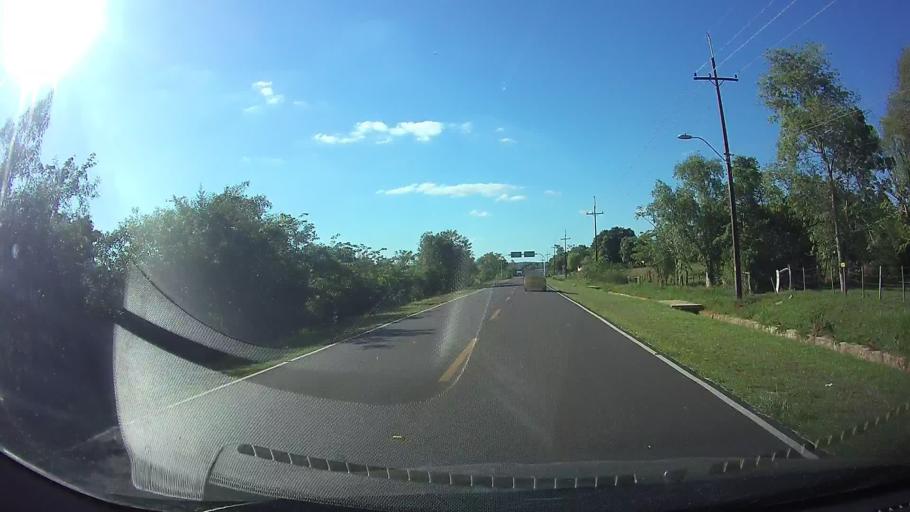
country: PY
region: Cordillera
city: Atyra
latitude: -25.2898
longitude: -57.1683
